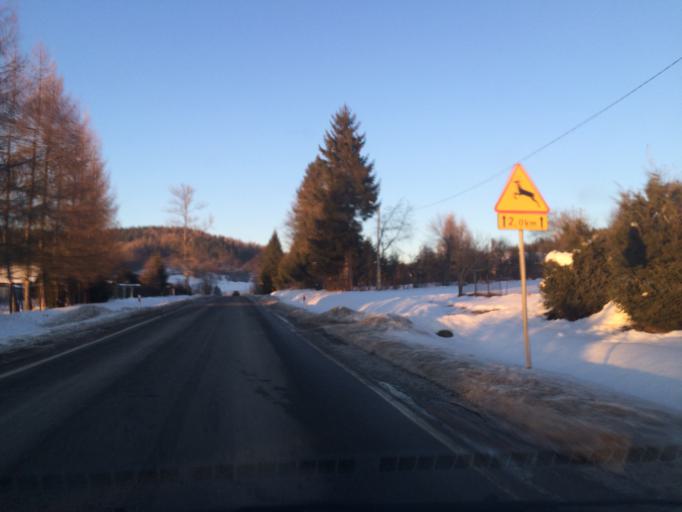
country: PL
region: Subcarpathian Voivodeship
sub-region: Powiat bieszczadzki
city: Czarna
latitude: 49.3369
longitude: 22.6728
